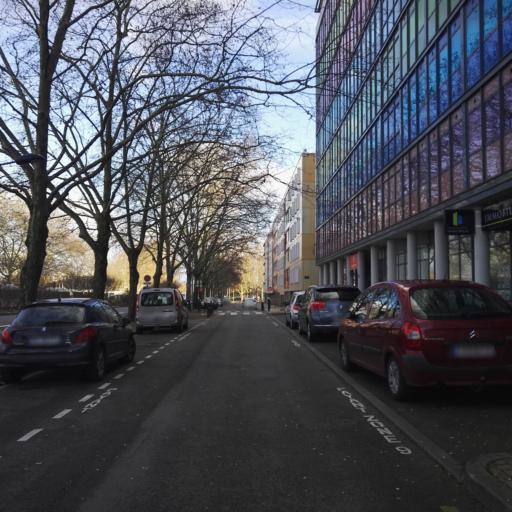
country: FR
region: Aquitaine
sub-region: Departement de la Gironde
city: Bordeaux
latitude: 44.8330
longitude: -0.5972
